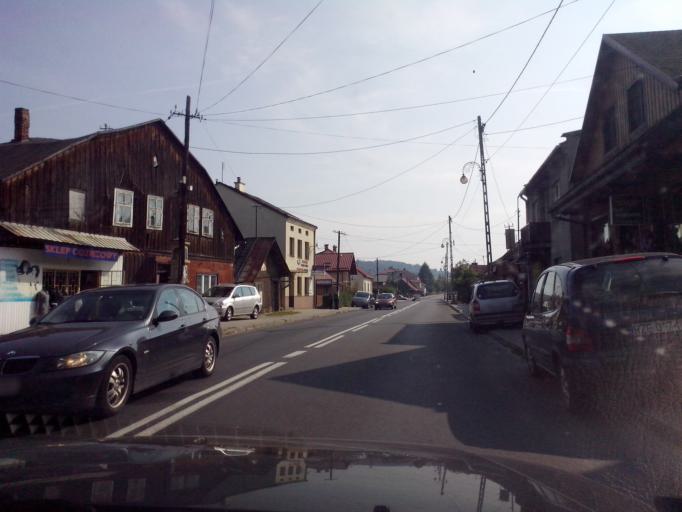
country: PL
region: Subcarpathian Voivodeship
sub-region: Powiat strzyzowski
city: Czudec
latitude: 49.9453
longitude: 21.8389
